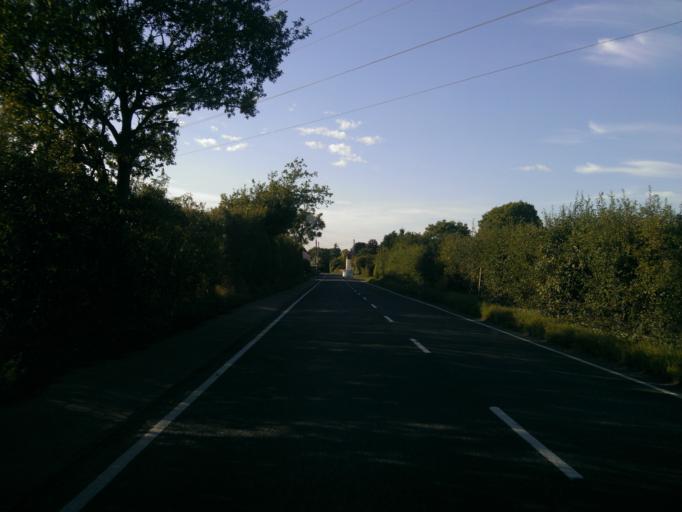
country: GB
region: England
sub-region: Essex
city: Alresford
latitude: 51.8605
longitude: 0.9970
